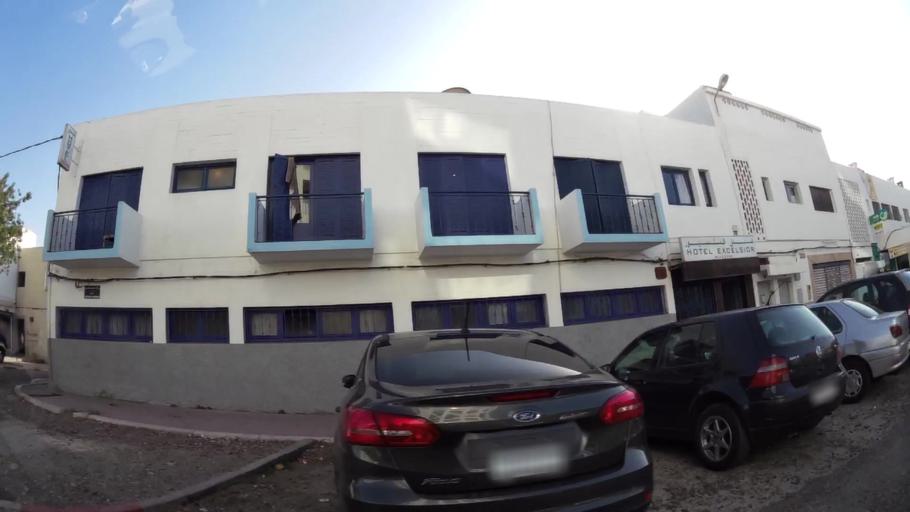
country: MA
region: Souss-Massa-Draa
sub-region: Agadir-Ida-ou-Tnan
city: Agadir
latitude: 30.4254
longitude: -9.5930
